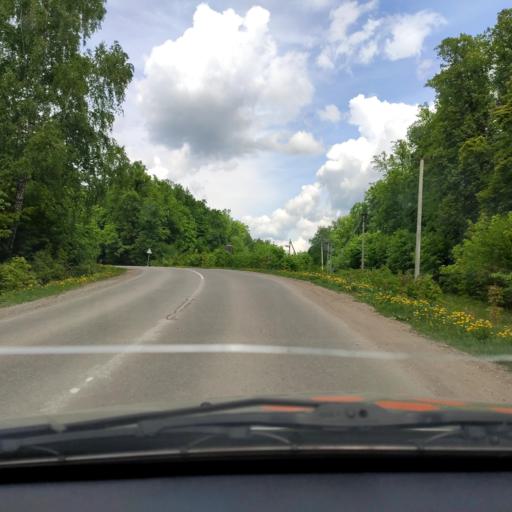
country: RU
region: Bashkortostan
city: Avdon
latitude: 54.6526
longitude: 55.7022
